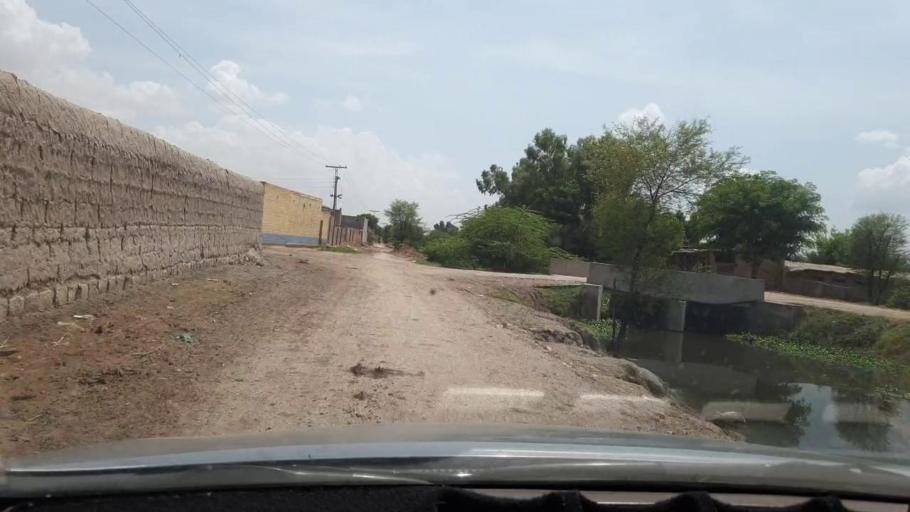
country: PK
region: Sindh
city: Khairpur
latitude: 27.4716
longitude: 68.7981
